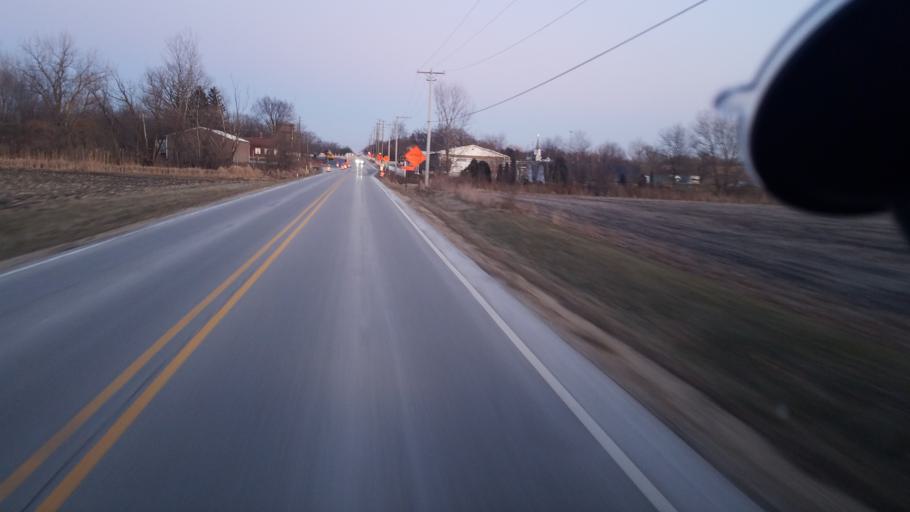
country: US
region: Illinois
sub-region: Kane County
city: Hampshire
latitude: 42.1608
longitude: -88.5318
